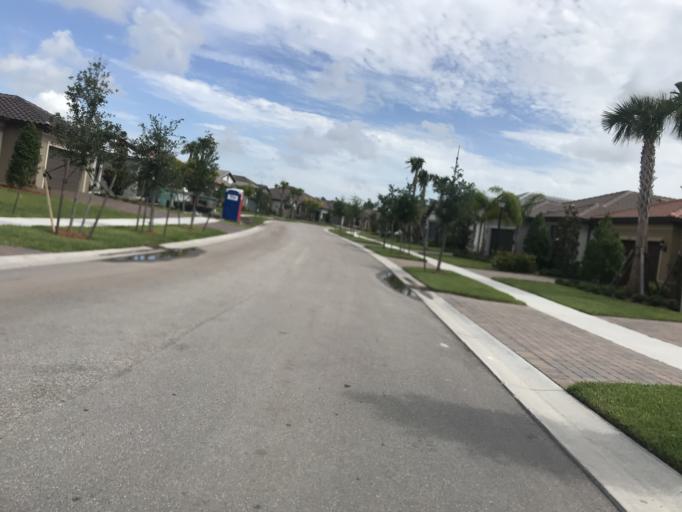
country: US
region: Florida
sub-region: Indian River County
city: Gifford
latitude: 27.6850
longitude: -80.4353
